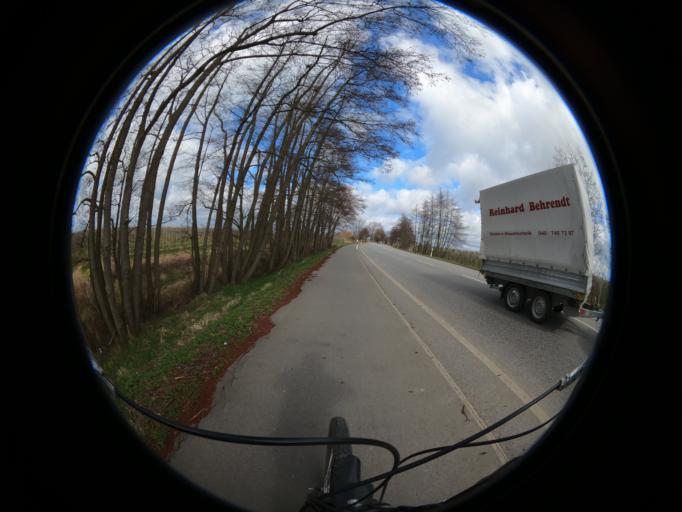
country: DE
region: Lower Saxony
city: Neu Wulmstorf
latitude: 53.5024
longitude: 9.7843
